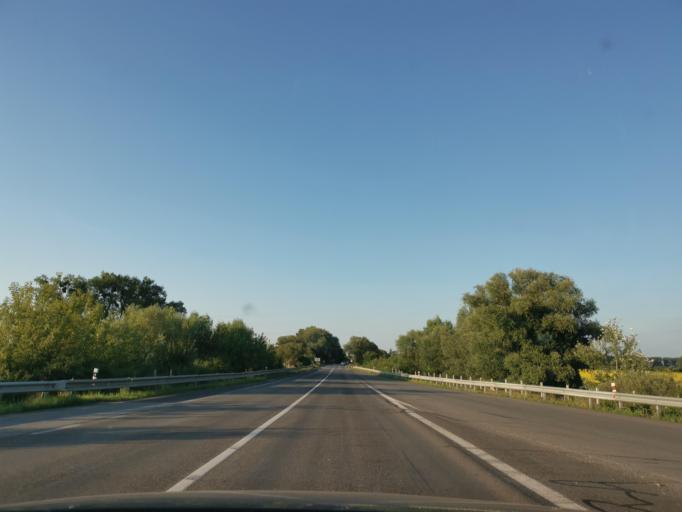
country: CZ
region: South Moravian
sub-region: Okres Breclav
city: Lanzhot
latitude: 48.6410
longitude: 17.0039
